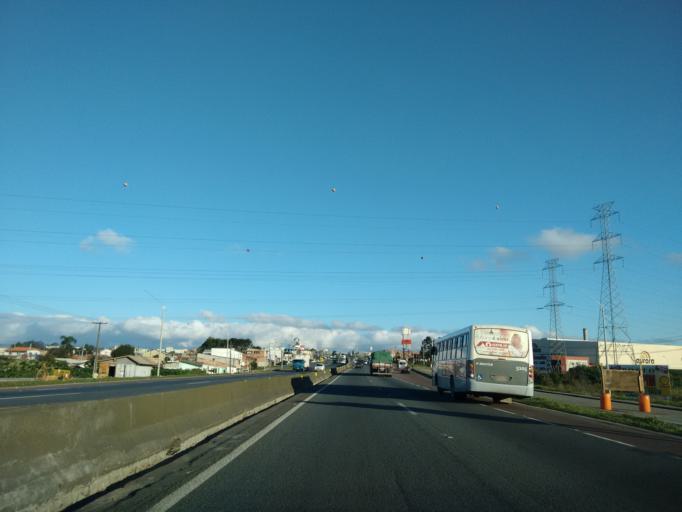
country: BR
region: Parana
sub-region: Sao Jose Dos Pinhais
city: Sao Jose dos Pinhais
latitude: -25.5995
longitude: -49.1736
